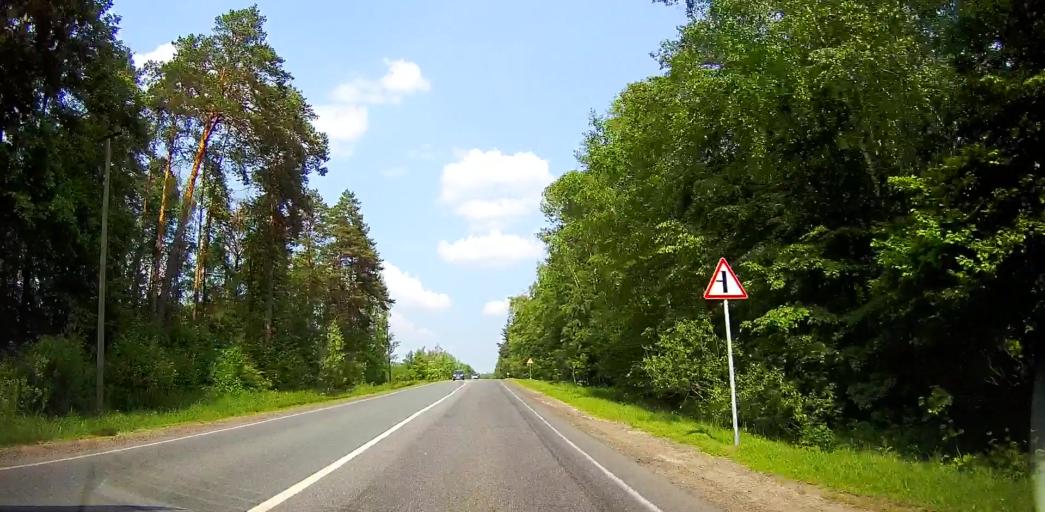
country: RU
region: Moskovskaya
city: Stupino
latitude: 54.9742
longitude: 38.1542
